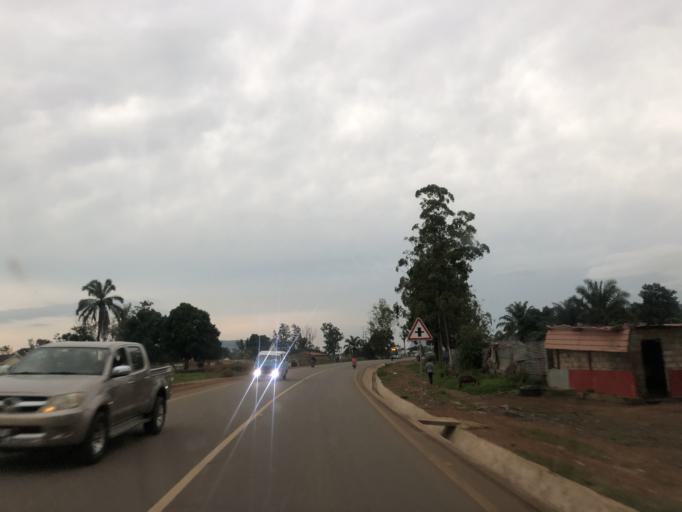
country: AO
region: Cuanza Sul
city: Uacu Cungo
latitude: -11.3531
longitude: 15.1202
